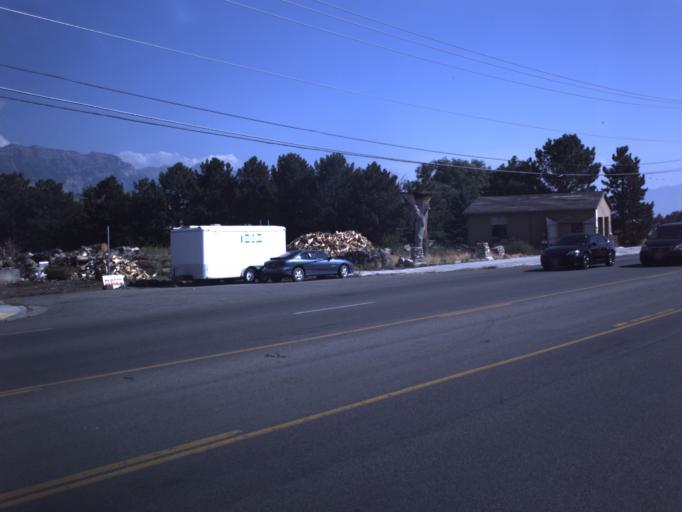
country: US
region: Utah
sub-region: Utah County
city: Cedar Hills
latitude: 40.4012
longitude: -111.7734
